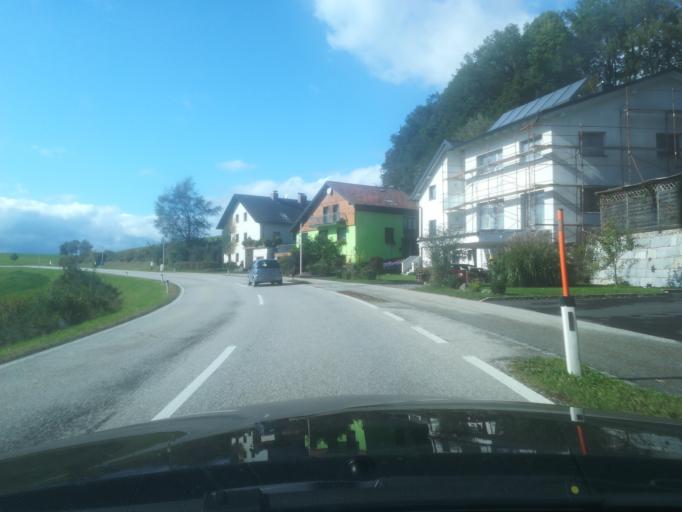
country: AT
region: Upper Austria
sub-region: Politischer Bezirk Urfahr-Umgebung
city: Eidenberg
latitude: 48.3635
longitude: 14.2489
